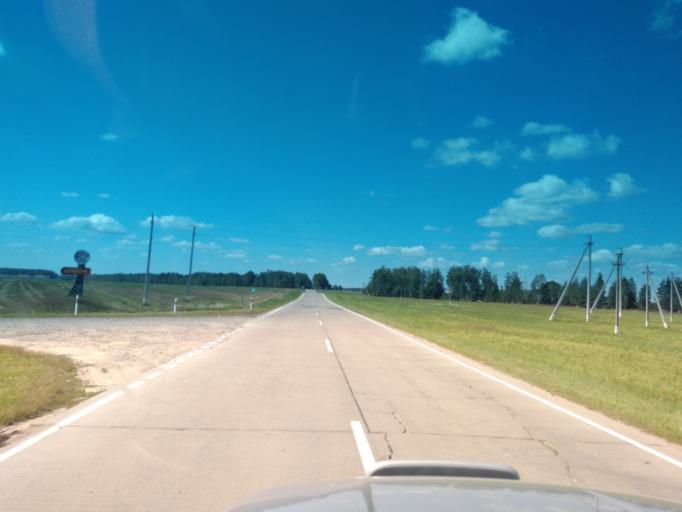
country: BY
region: Minsk
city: Stan'kava
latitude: 53.6261
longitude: 27.2658
